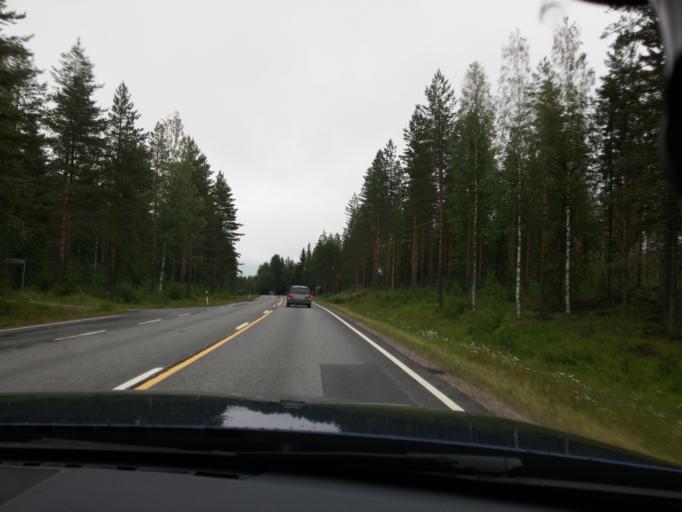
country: FI
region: Pirkanmaa
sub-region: Ylae-Pirkanmaa
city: Maenttae
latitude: 61.9611
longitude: 24.5890
